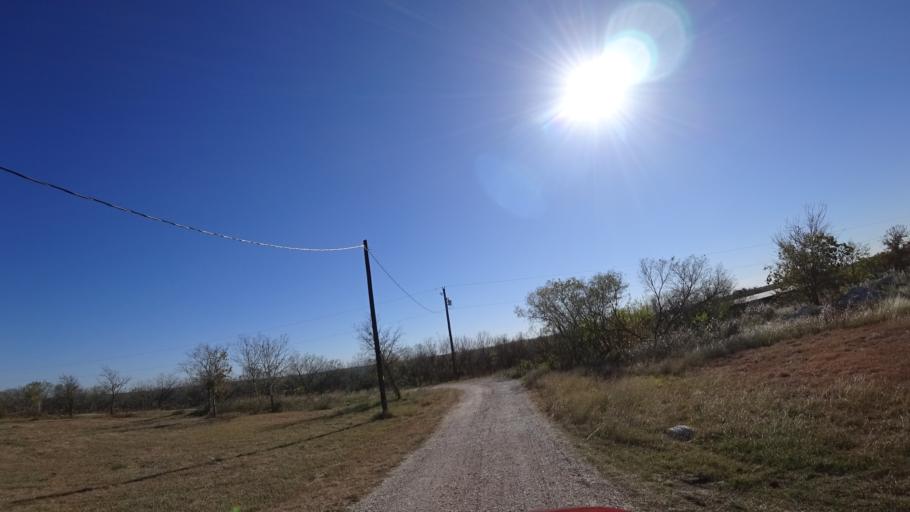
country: US
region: Texas
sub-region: Travis County
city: Garfield
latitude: 30.1189
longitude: -97.6293
